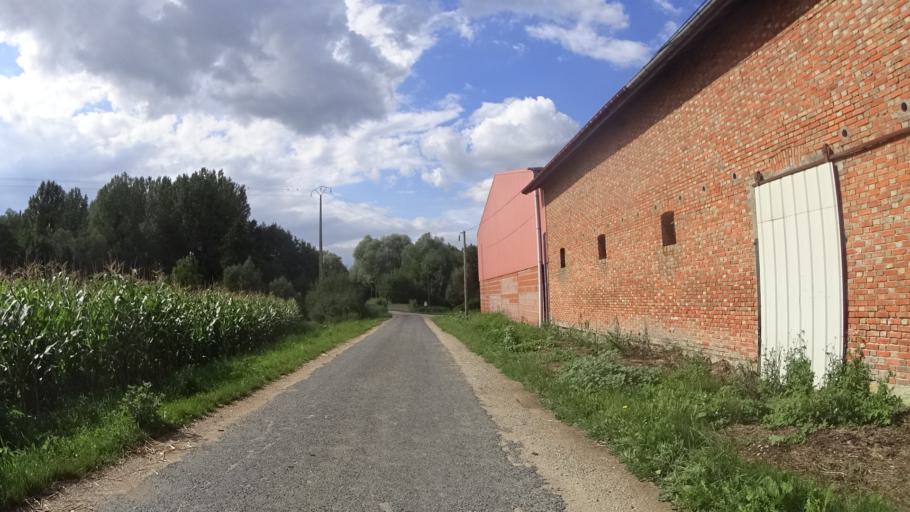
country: FR
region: Champagne-Ardenne
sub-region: Departement de la Marne
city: Pargny-sur-Saulx
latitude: 48.7760
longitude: 4.8584
